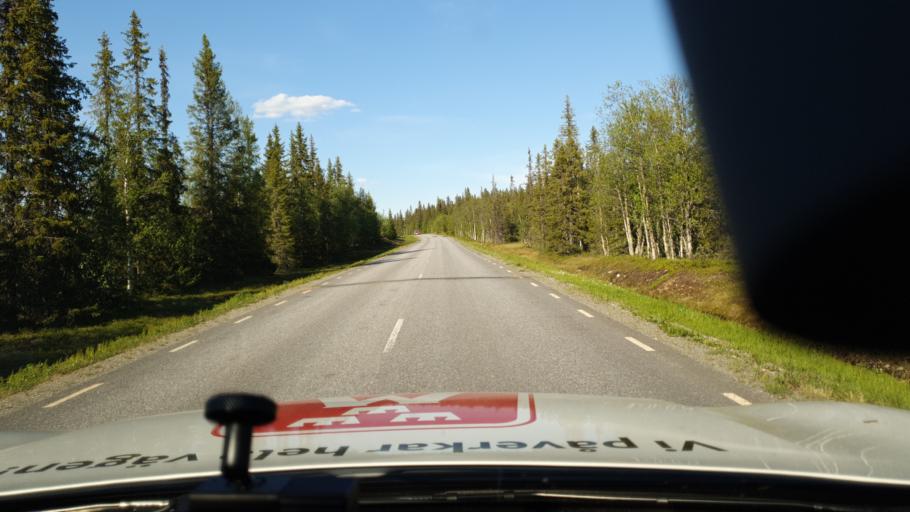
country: SE
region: Vaesterbotten
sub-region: Asele Kommun
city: Insjon
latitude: 64.7225
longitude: 17.3408
